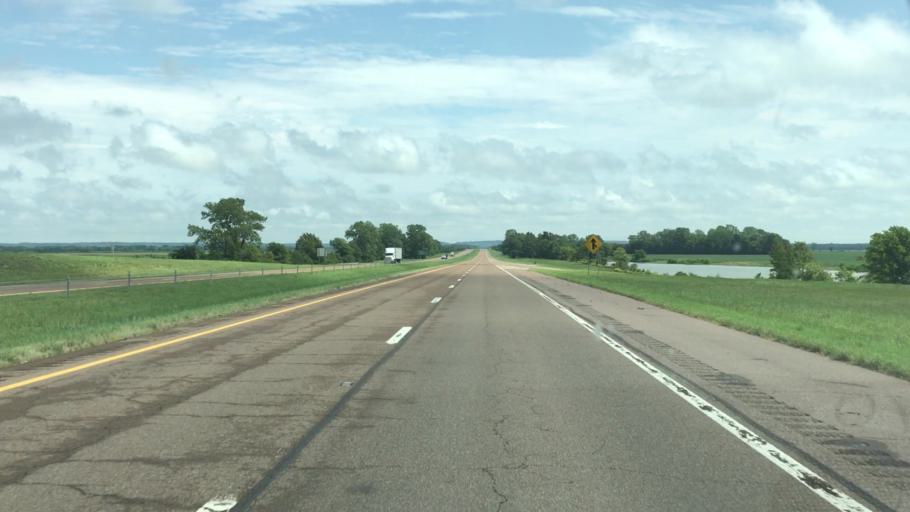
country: US
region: Missouri
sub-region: Pemiscot County
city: Caruthersville
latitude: 36.0927
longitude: -89.5844
